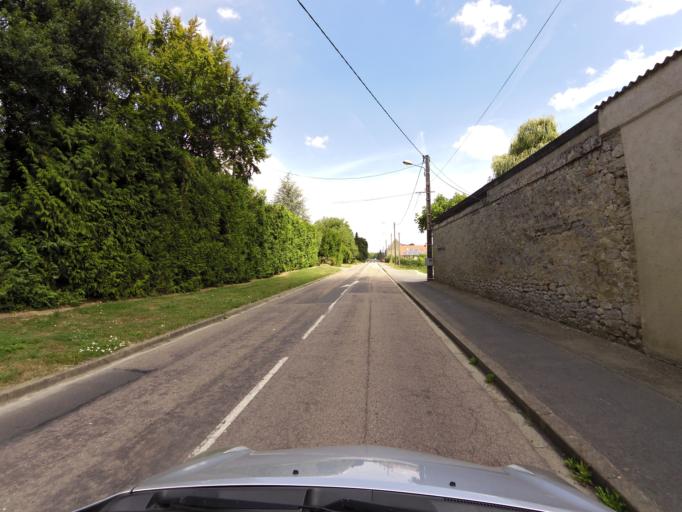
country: FR
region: Picardie
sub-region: Departement de l'Oise
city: Mareuil-sur-Ourcq
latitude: 49.1162
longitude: 3.0631
